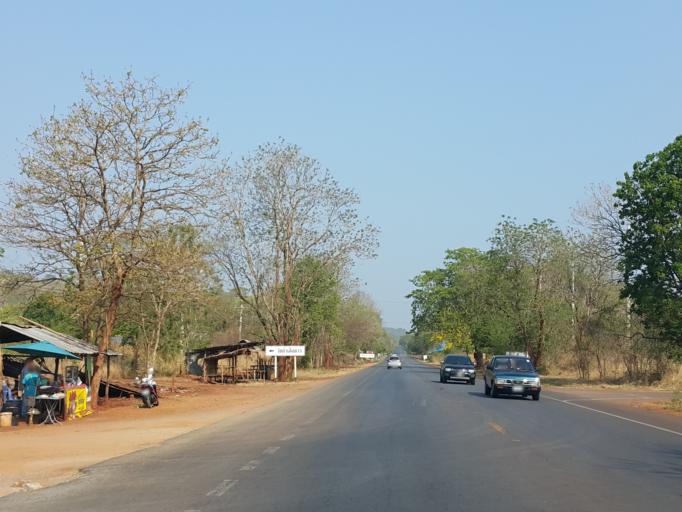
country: TH
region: Kanchanaburi
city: Sai Yok
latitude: 14.1007
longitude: 99.2301
